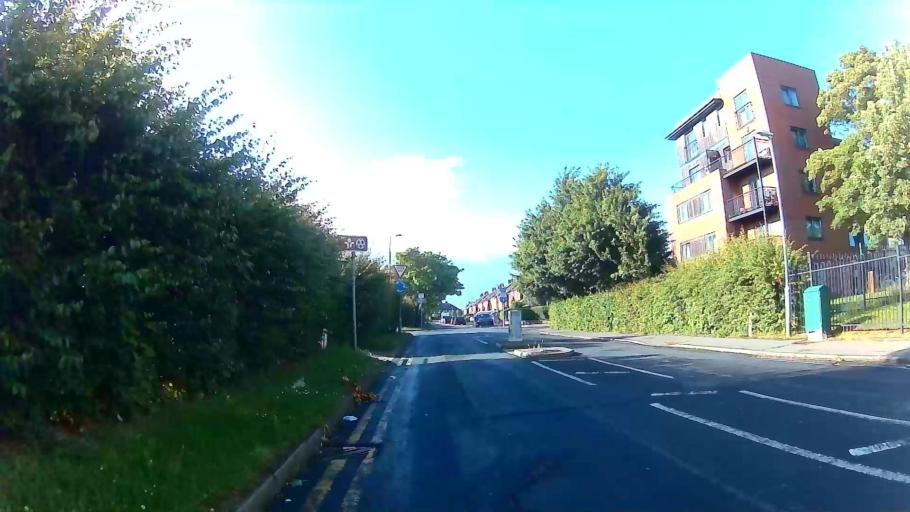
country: GB
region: England
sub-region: Essex
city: Chelmsford
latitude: 51.7494
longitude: 0.4514
